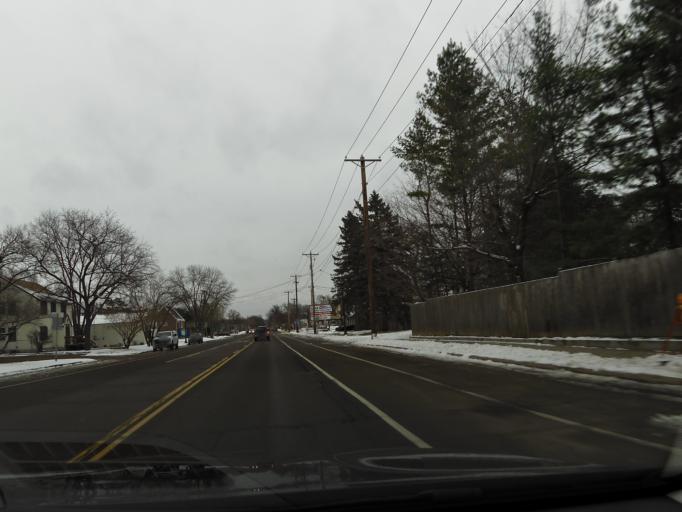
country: US
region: Minnesota
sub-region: Dakota County
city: West Saint Paul
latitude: 44.9306
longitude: -93.1385
